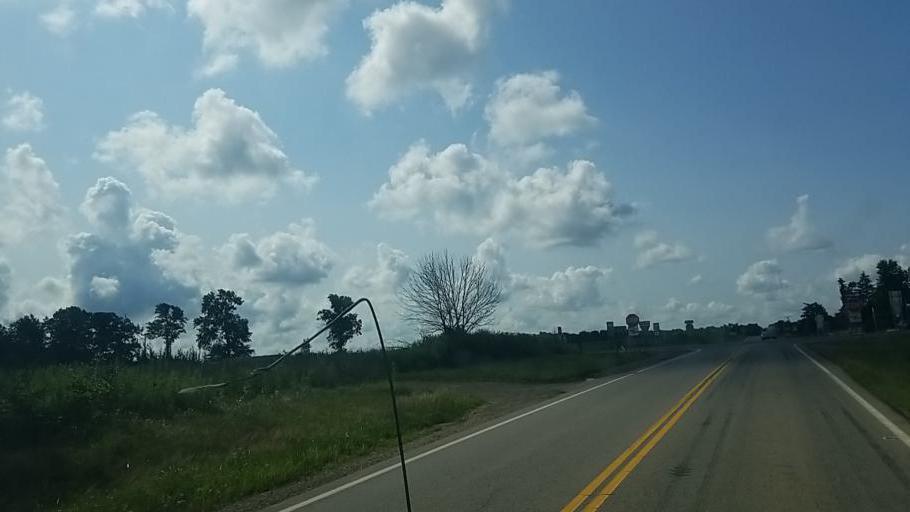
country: US
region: Ohio
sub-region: Ashland County
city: Ashland
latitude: 40.7856
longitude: -82.3064
